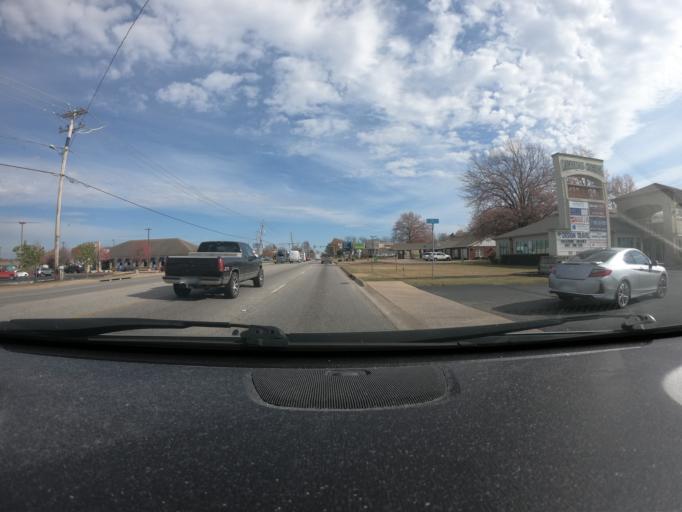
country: US
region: Arkansas
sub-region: Benton County
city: Rogers
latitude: 36.3340
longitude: -94.1453
